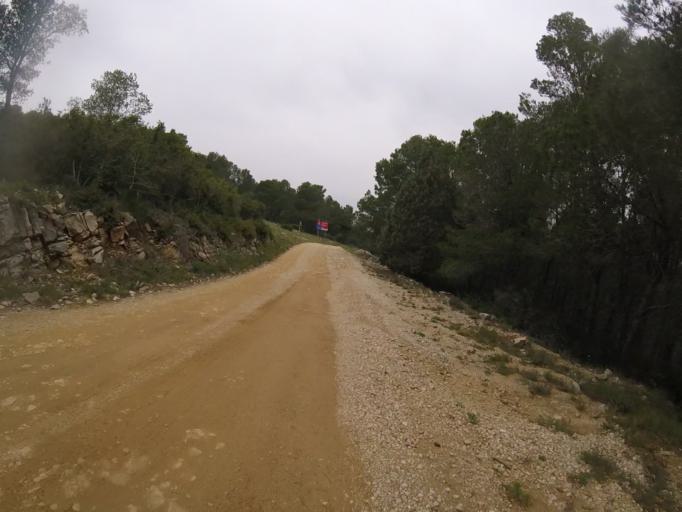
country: ES
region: Valencia
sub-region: Provincia de Castello
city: Alcala de Xivert
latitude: 40.3055
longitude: 0.2563
